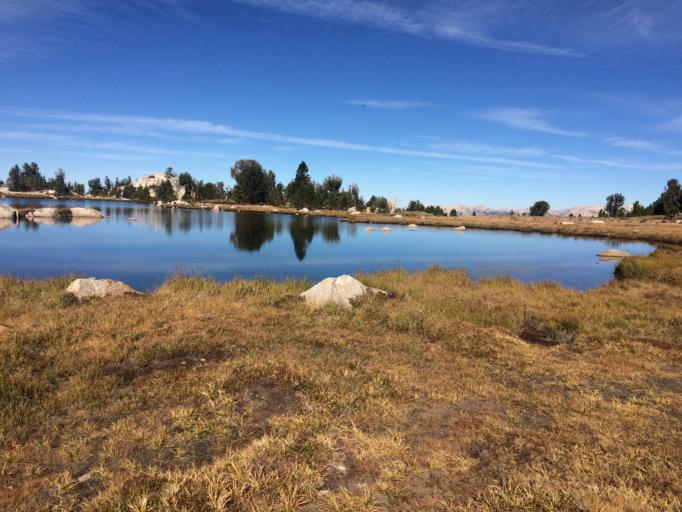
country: US
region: California
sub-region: Mariposa County
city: Yosemite Valley
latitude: 37.9368
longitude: -119.3343
